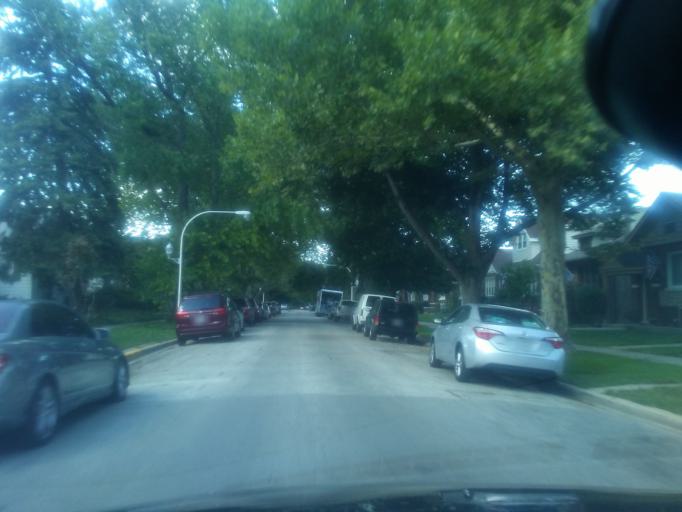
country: US
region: Illinois
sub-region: Cook County
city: Lincolnwood
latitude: 41.9727
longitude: -87.7331
